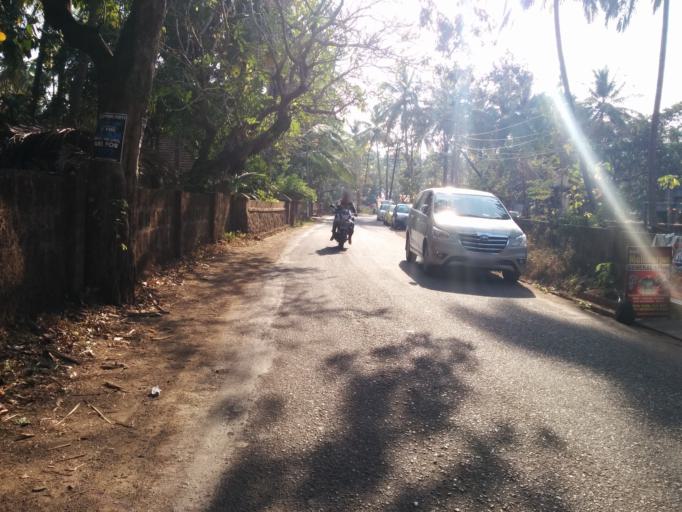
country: IN
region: Goa
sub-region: South Goa
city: Kankon
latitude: 15.0106
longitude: 74.0276
